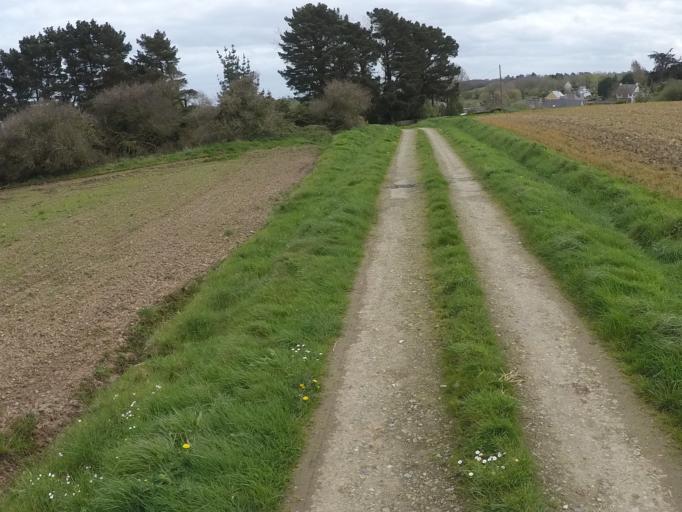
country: FR
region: Brittany
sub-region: Departement des Cotes-d'Armor
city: Plouezec
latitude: 48.7227
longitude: -2.9539
